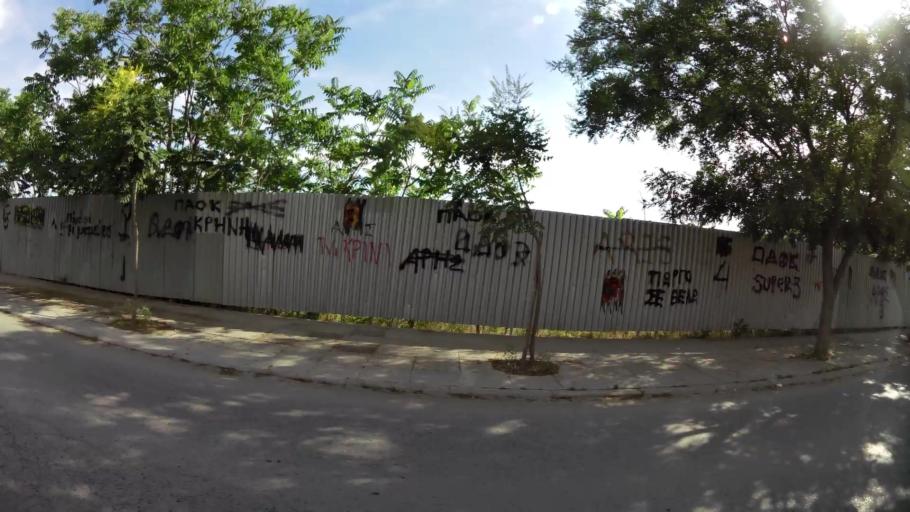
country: GR
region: Central Macedonia
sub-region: Nomos Thessalonikis
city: Kalamaria
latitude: 40.5669
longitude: 22.9651
